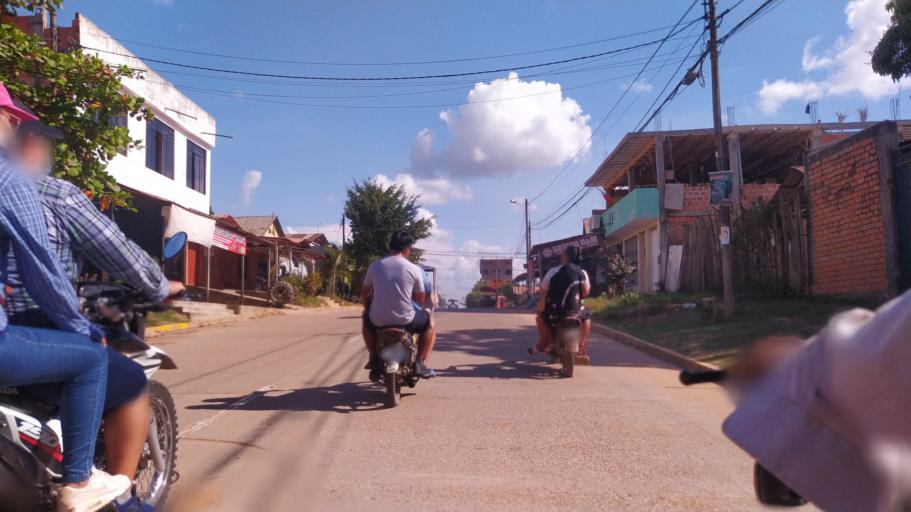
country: PE
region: Ucayali
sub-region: Provincia de Coronel Portillo
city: Puerto Callao
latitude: -8.3572
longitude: -74.5808
